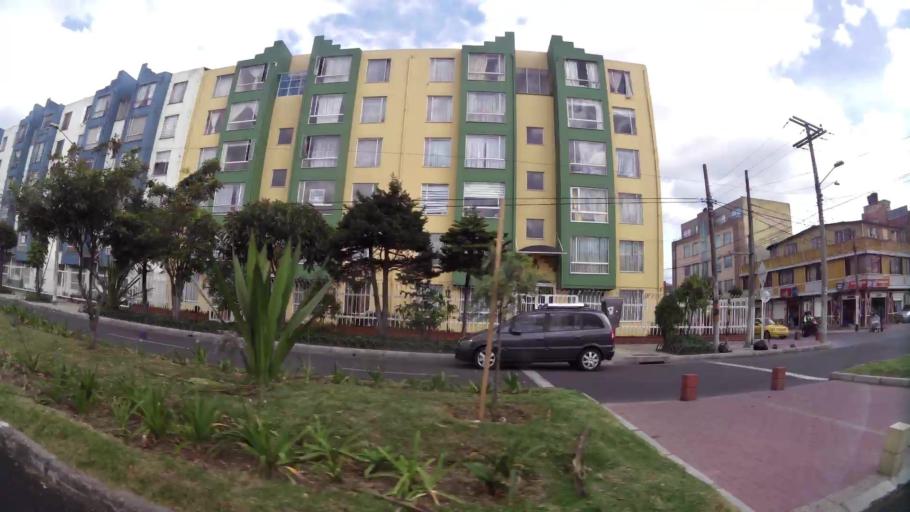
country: CO
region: Bogota D.C.
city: Bogota
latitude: 4.6098
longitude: -74.1353
